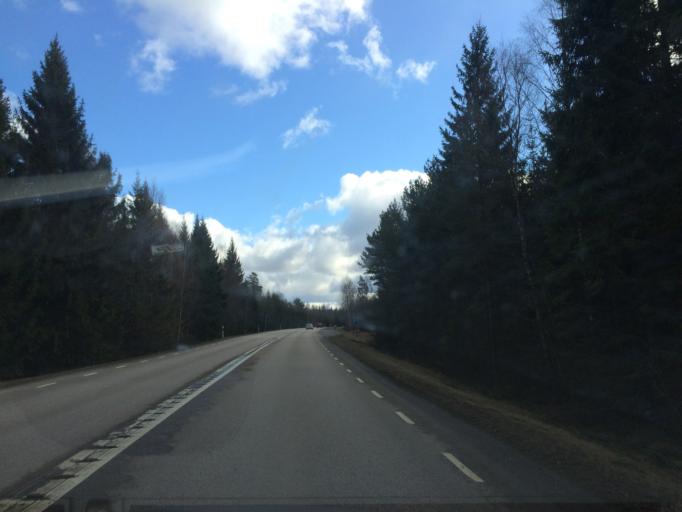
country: SE
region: Vaestra Goetaland
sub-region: Skara Kommun
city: Skara
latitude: 58.3084
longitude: 13.4635
